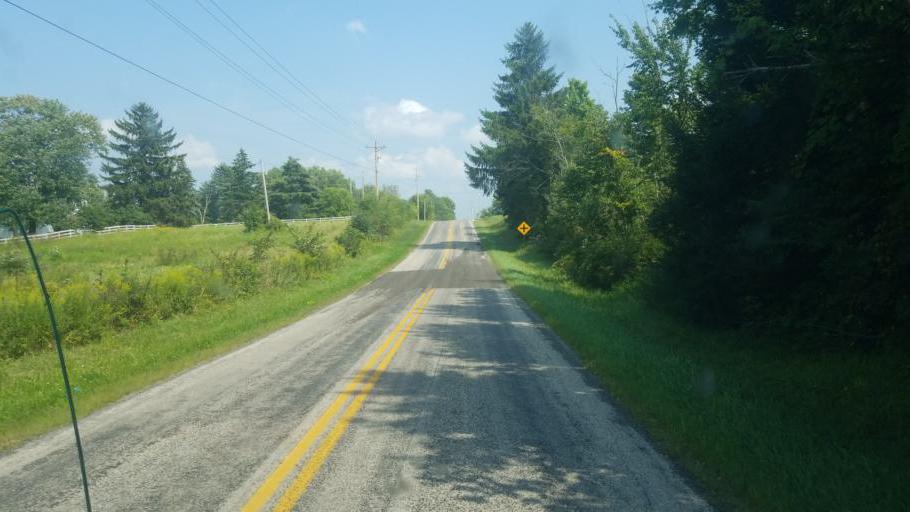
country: US
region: Ohio
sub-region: Huron County
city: New London
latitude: 41.0657
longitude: -82.3778
